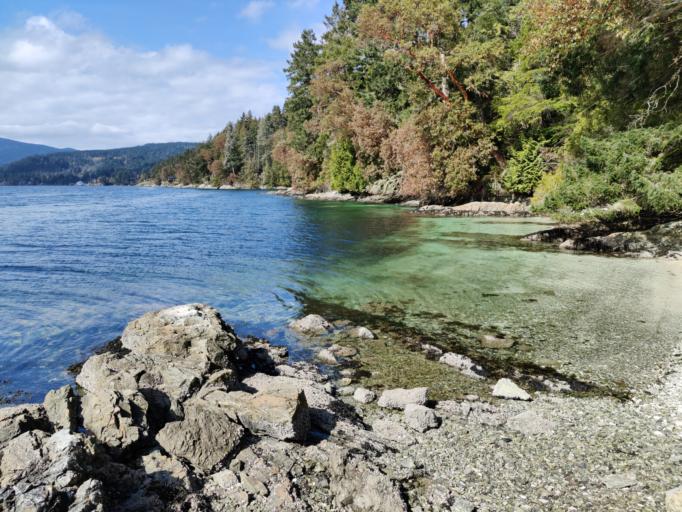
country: CA
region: British Columbia
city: North Saanich
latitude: 48.7572
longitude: -123.4330
